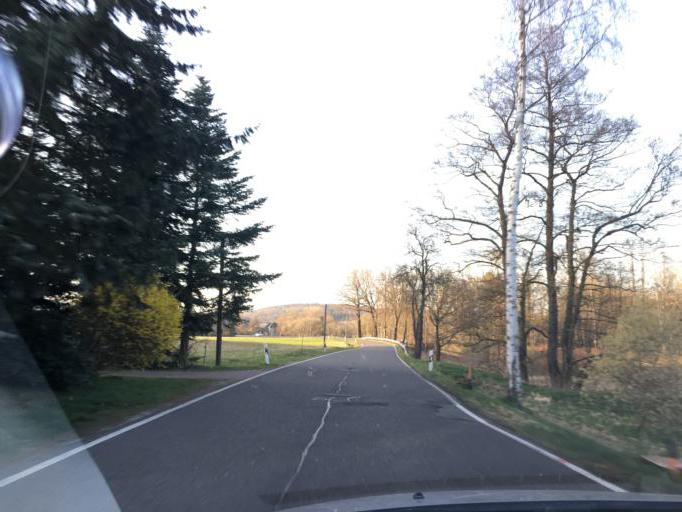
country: DE
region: Saxony
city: Wechselburg
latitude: 50.9894
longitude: 12.7734
